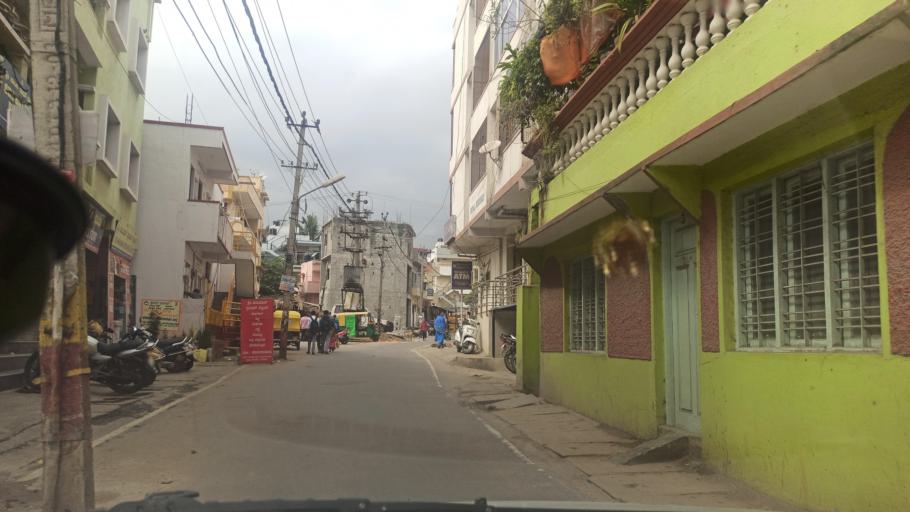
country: IN
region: Karnataka
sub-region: Bangalore Urban
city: Bangalore
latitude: 13.0358
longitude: 77.5976
